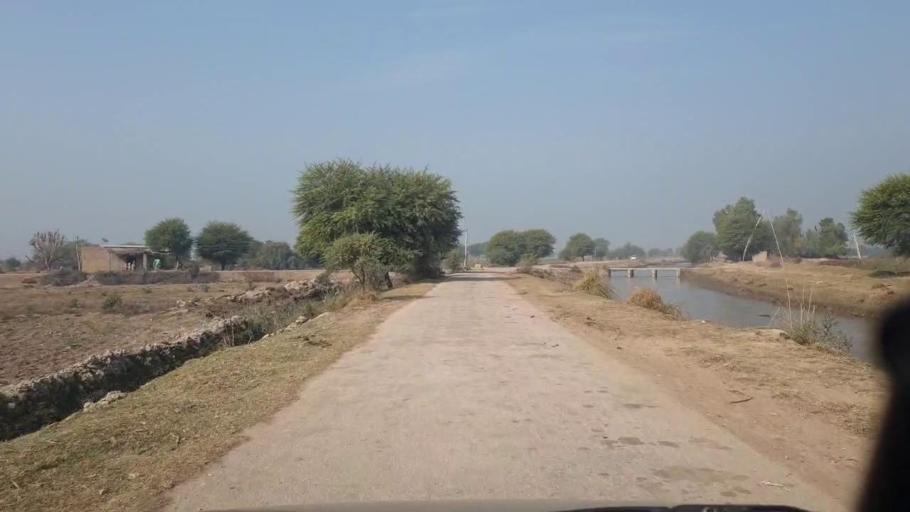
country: PK
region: Sindh
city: Shahdadpur
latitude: 26.0342
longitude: 68.5345
